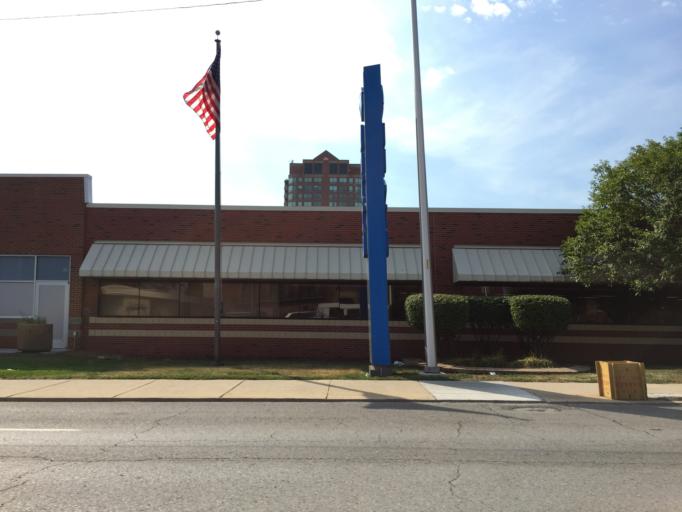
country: US
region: Michigan
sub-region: Wayne County
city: Detroit
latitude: 42.3419
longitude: -83.0142
